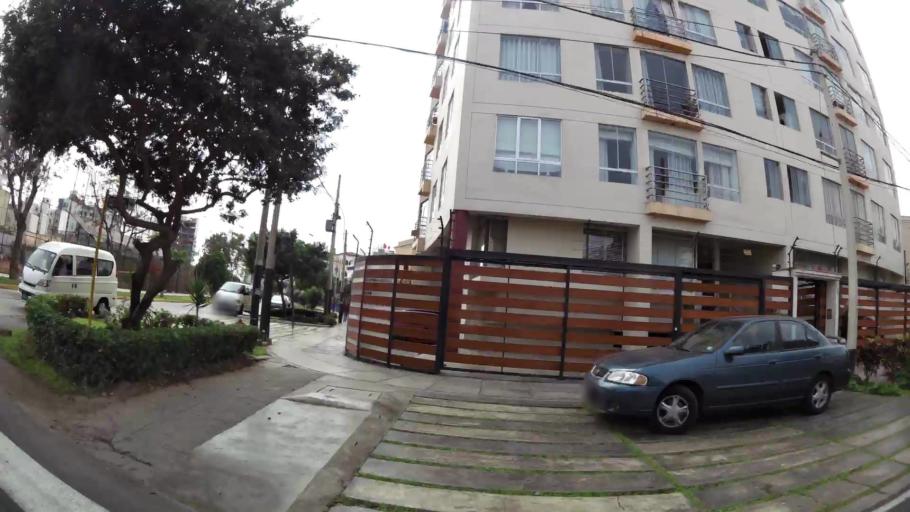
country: PE
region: Lima
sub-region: Lima
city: San Isidro
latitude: -12.0817
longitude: -77.0538
